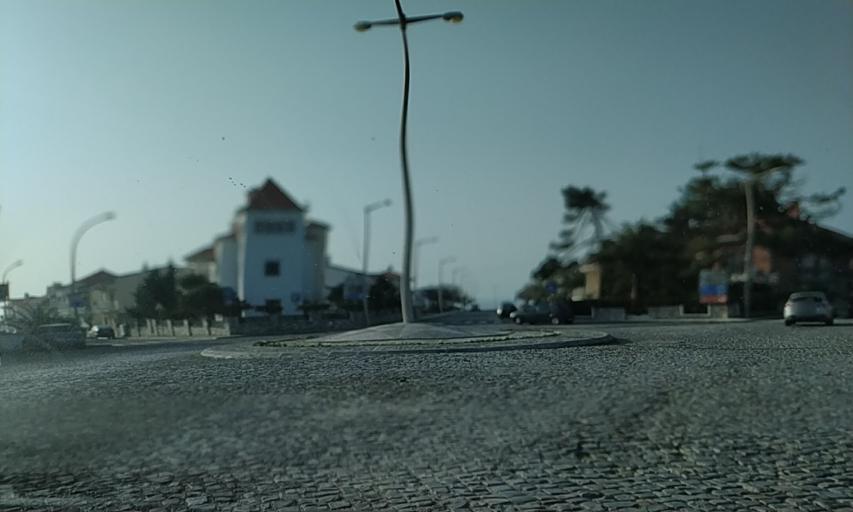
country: PT
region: Leiria
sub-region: Alcobaca
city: Pataias
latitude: 39.7578
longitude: -9.0295
